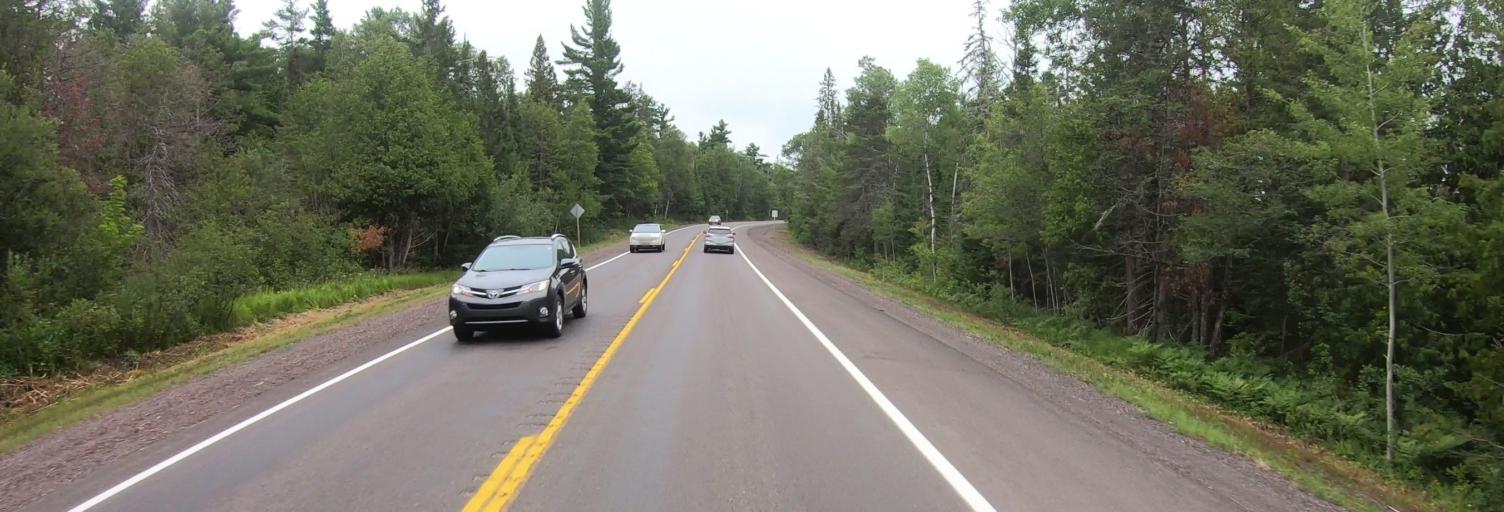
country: US
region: Michigan
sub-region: Keweenaw County
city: Eagle River
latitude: 47.3733
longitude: -88.3045
